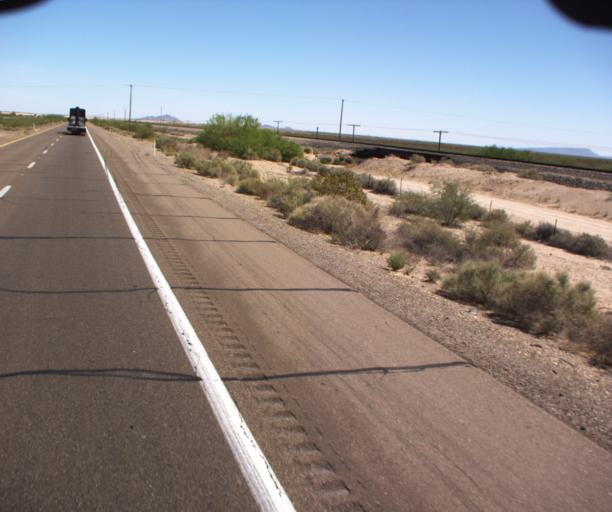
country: US
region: Arizona
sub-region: Yuma County
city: Wellton
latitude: 32.7499
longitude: -113.6629
